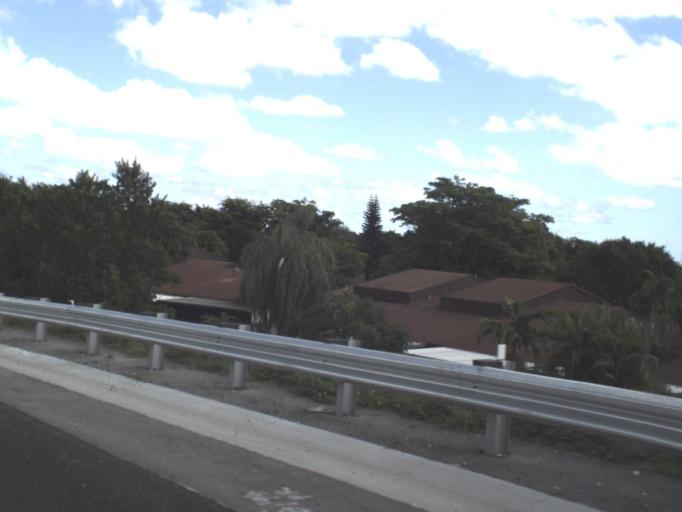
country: US
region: Florida
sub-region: Broward County
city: Miramar
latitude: 25.9745
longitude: -80.2286
